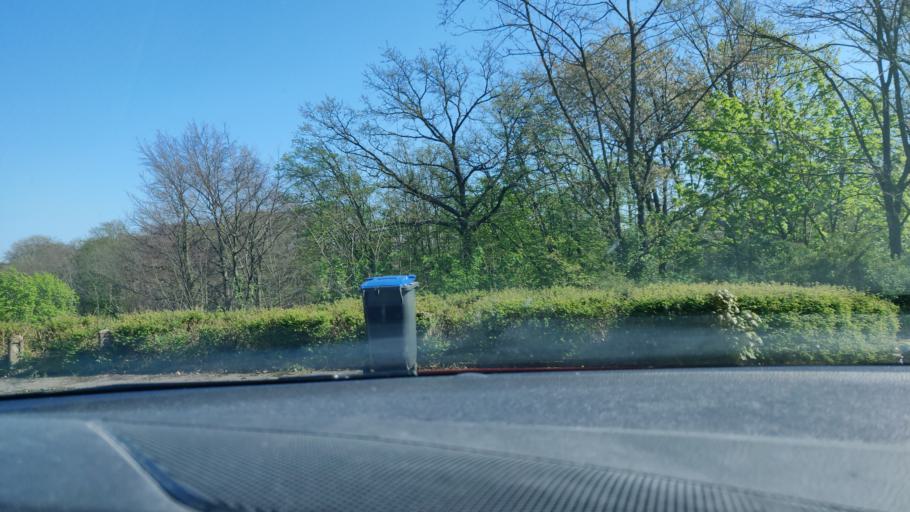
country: DE
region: North Rhine-Westphalia
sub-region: Regierungsbezirk Dusseldorf
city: Velbert
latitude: 51.3477
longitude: 7.0322
